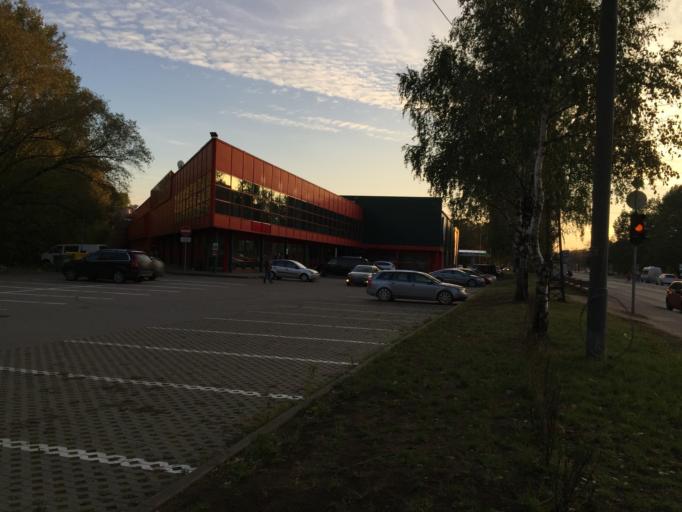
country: LV
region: Riga
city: Riga
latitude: 56.9397
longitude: 24.0917
